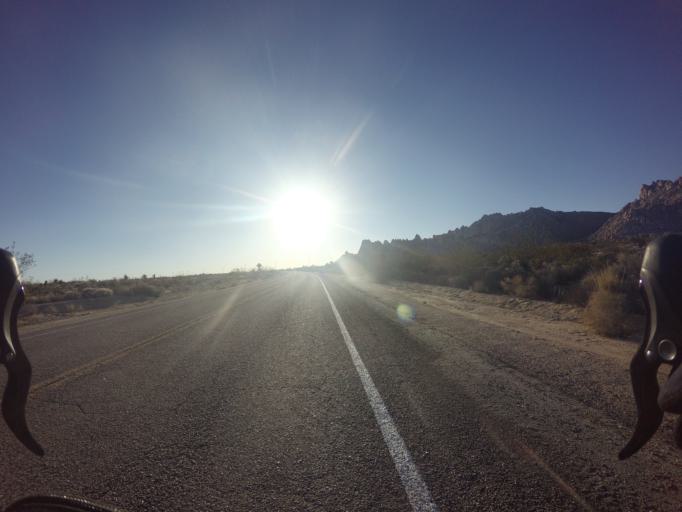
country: US
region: California
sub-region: San Bernardino County
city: Twentynine Palms
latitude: 34.7864
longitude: -115.6157
